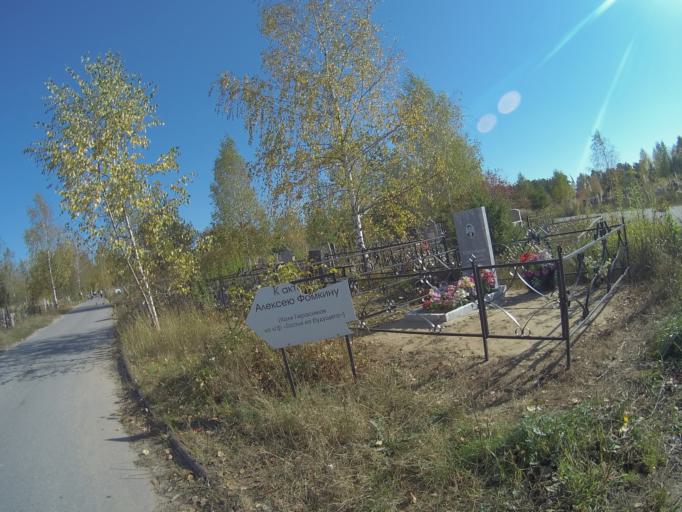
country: RU
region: Vladimir
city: Golovino
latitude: 56.0360
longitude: 40.4279
